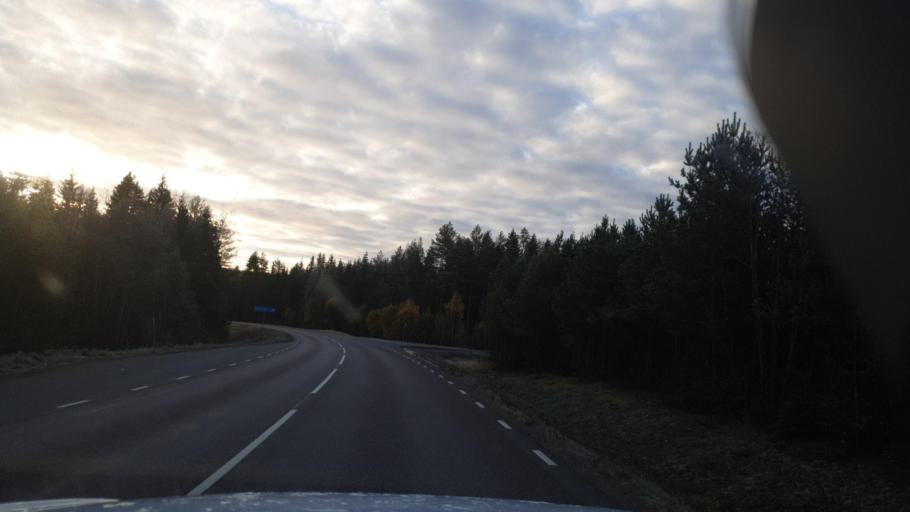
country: SE
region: Vaermland
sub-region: Eda Kommun
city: Amotfors
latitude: 59.7315
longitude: 12.1712
